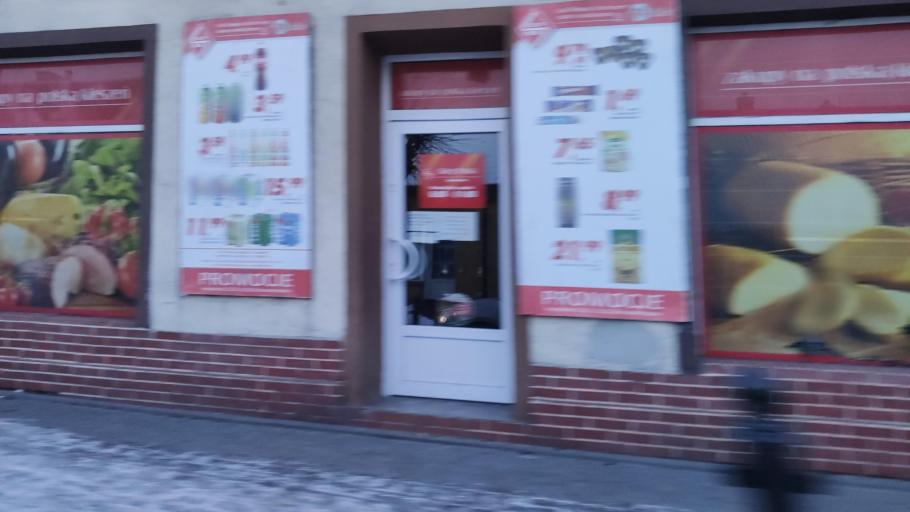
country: PL
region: Kujawsko-Pomorskie
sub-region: Powiat zninski
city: Barcin
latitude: 52.8634
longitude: 17.9465
